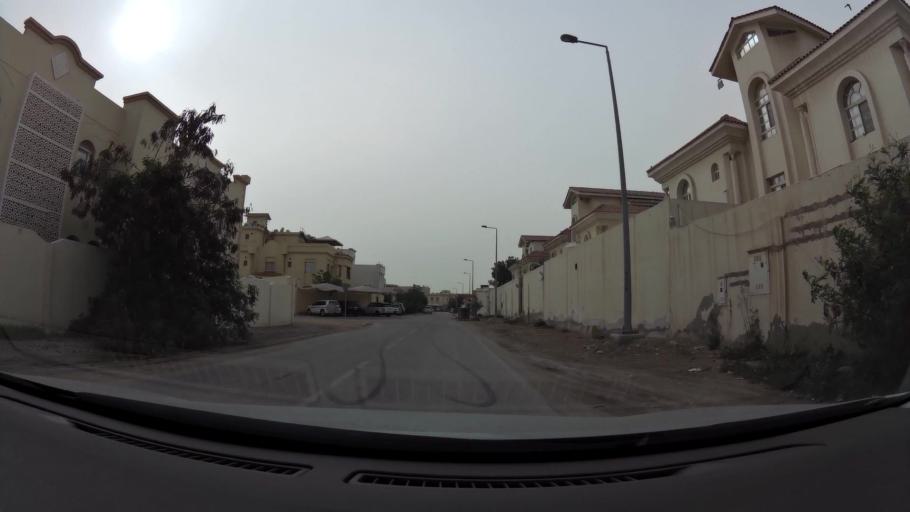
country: QA
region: Baladiyat ad Dawhah
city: Doha
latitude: 25.2428
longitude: 51.5022
